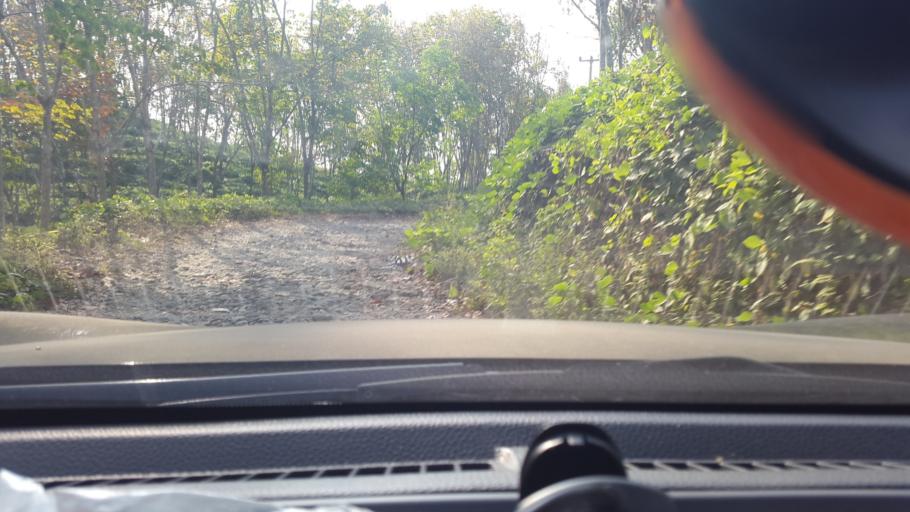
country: ID
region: West Java
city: Cikupa
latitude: -7.3597
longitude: 106.6964
